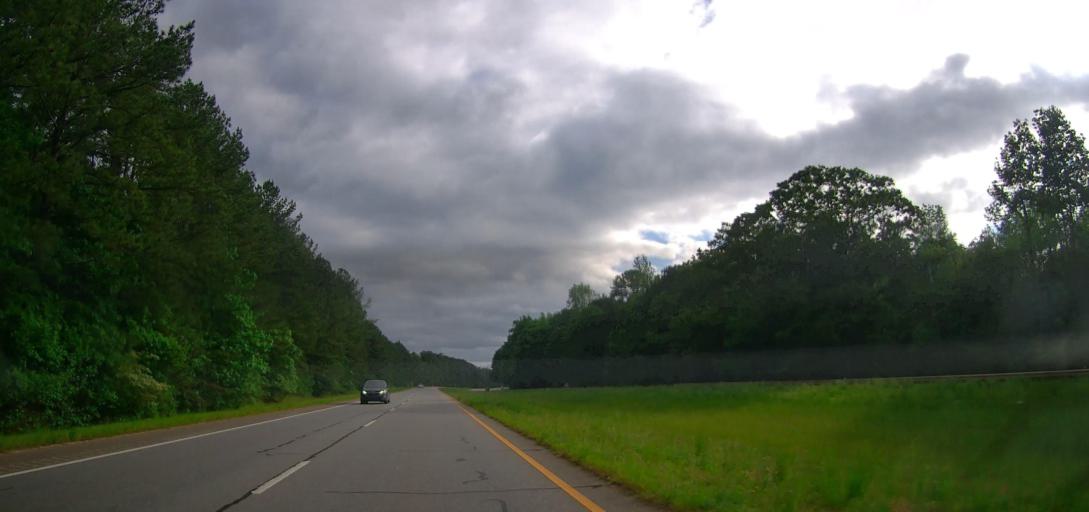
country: US
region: Georgia
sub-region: Barrow County
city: Statham
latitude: 33.8777
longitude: -83.5945
